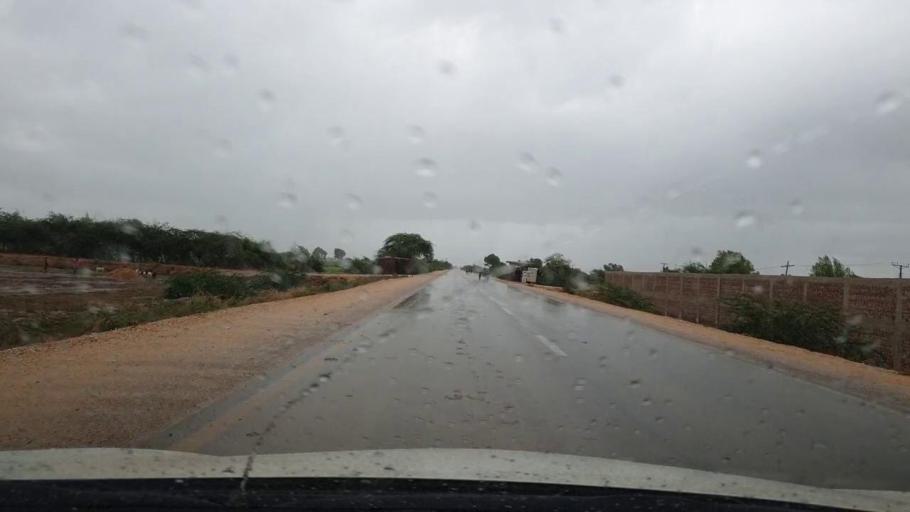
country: PK
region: Sindh
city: Kario
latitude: 24.6534
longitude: 68.5731
